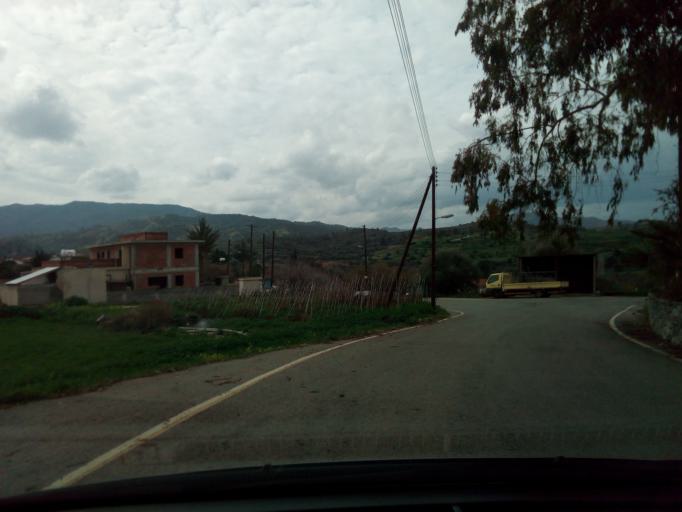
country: CY
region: Lefkosia
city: Lefka
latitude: 35.0678
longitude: 32.8878
